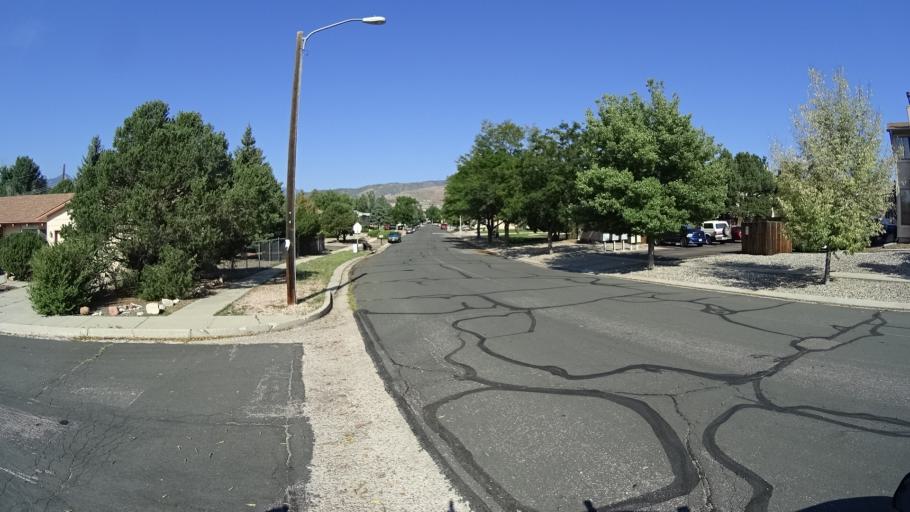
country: US
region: Colorado
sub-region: El Paso County
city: Colorado Springs
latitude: 38.8908
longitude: -104.8418
